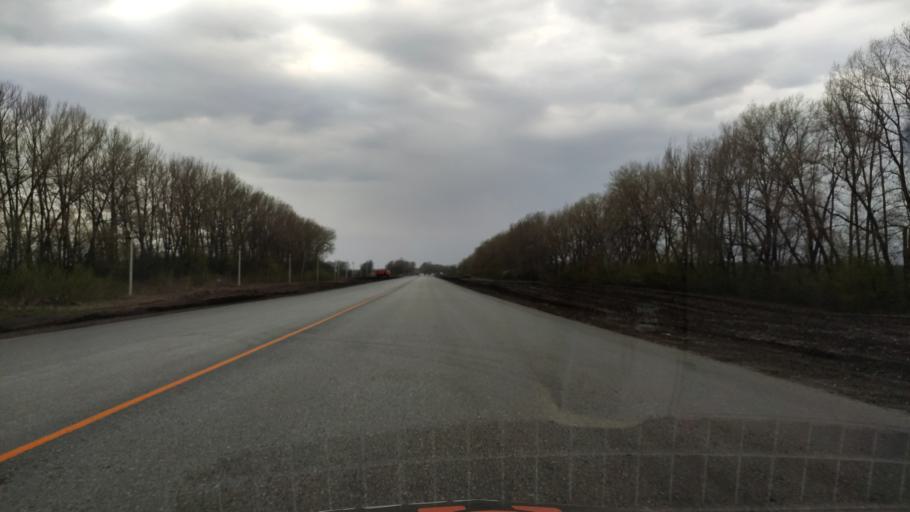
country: RU
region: Kursk
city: Gorshechnoye
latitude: 51.5477
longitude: 38.0803
